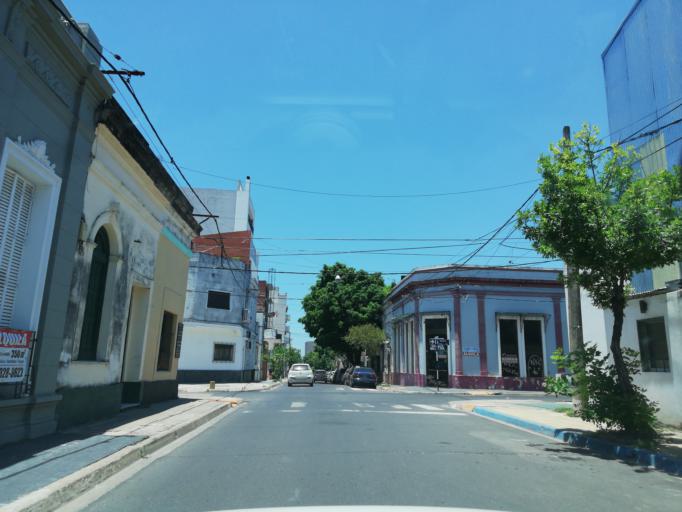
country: AR
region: Corrientes
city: Corrientes
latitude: -27.4649
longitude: -58.8304
